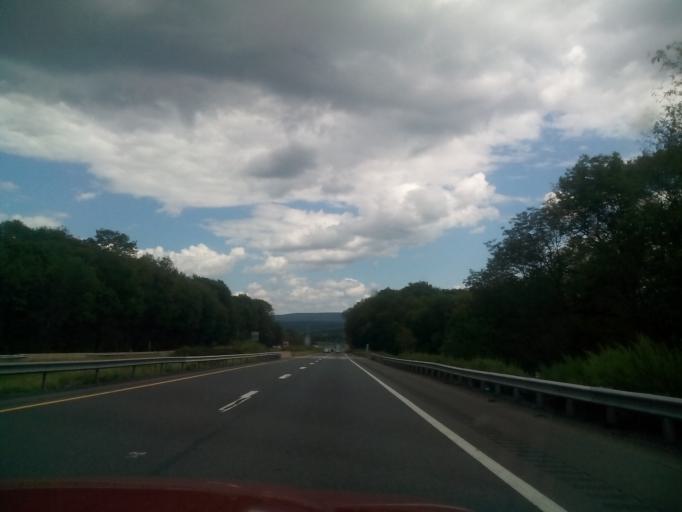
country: US
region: Pennsylvania
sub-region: Monroe County
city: Arlington Heights
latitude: 40.9896
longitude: -75.2447
